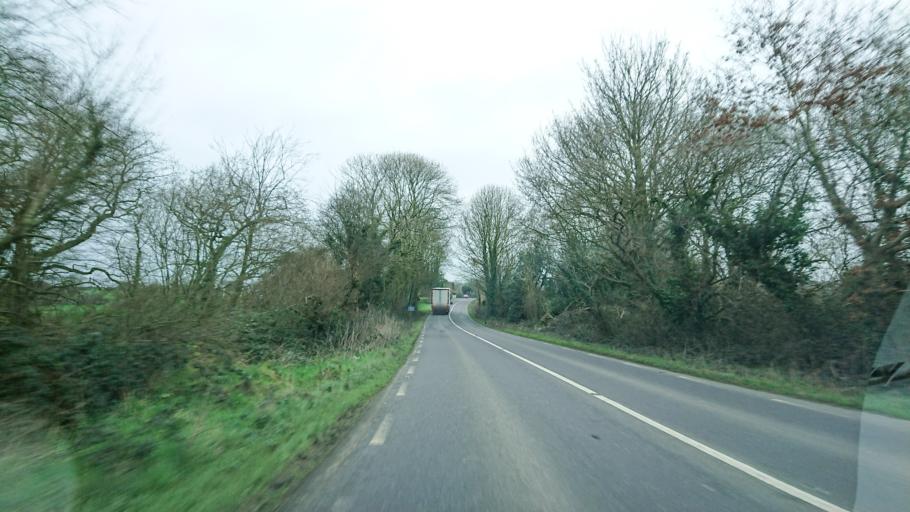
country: IE
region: Munster
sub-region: County Cork
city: Bandon
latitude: 51.7443
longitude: -8.8190
